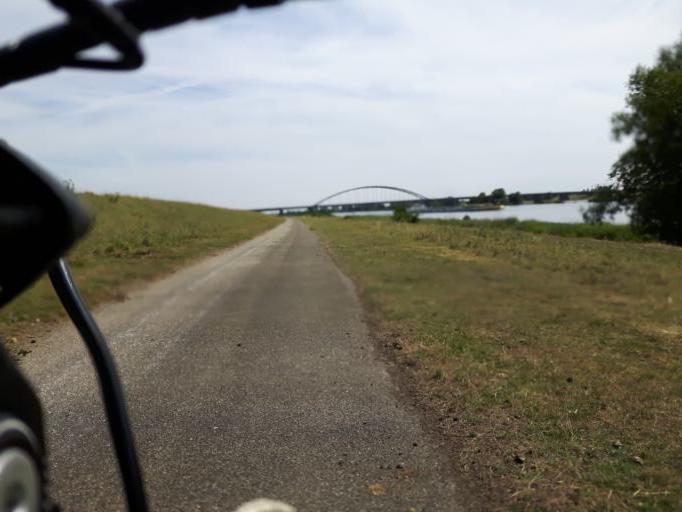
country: NL
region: North Brabant
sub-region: Gemeente Steenbergen
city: Nieuw-Vossemeer
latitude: 51.5897
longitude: 4.1974
